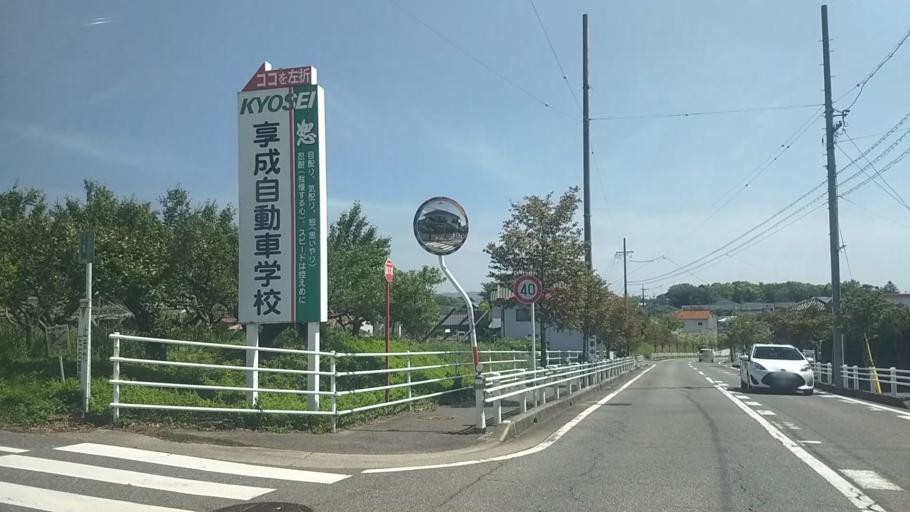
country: JP
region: Aichi
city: Okazaki
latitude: 34.9778
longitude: 137.1779
